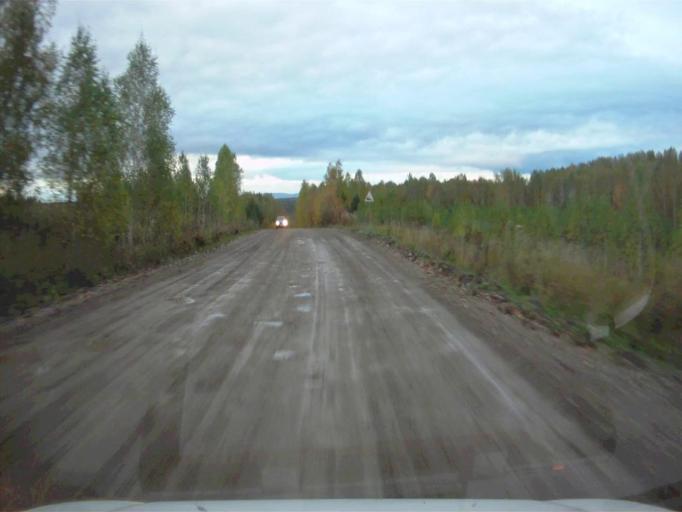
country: RU
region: Sverdlovsk
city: Mikhaylovsk
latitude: 56.2094
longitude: 59.2101
